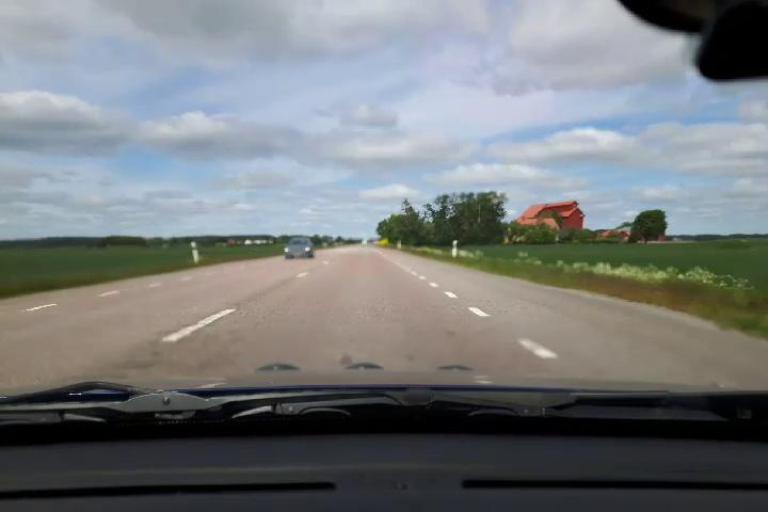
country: SE
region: Uppsala
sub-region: Uppsala Kommun
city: Gamla Uppsala
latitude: 59.9175
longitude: 17.6041
